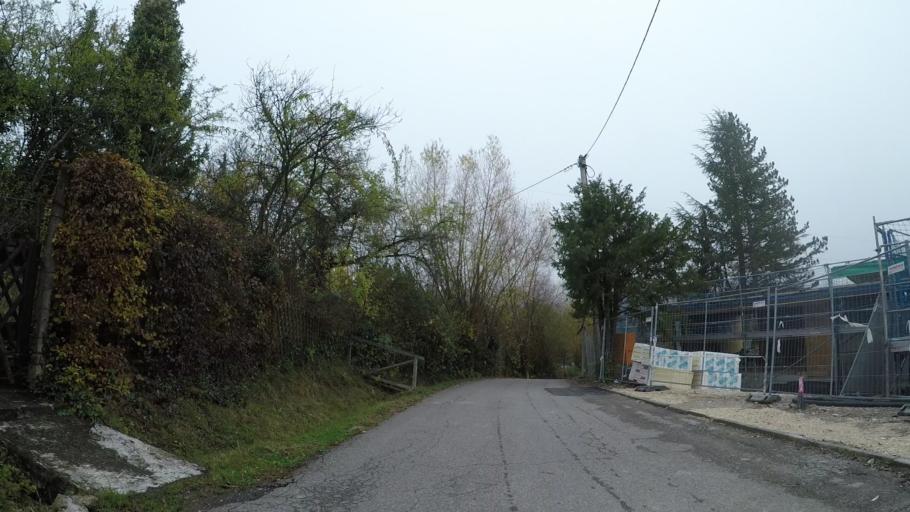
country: DE
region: Baden-Wuerttemberg
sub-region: Tuebingen Region
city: Eningen unter Achalm
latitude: 48.4882
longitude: 9.2399
